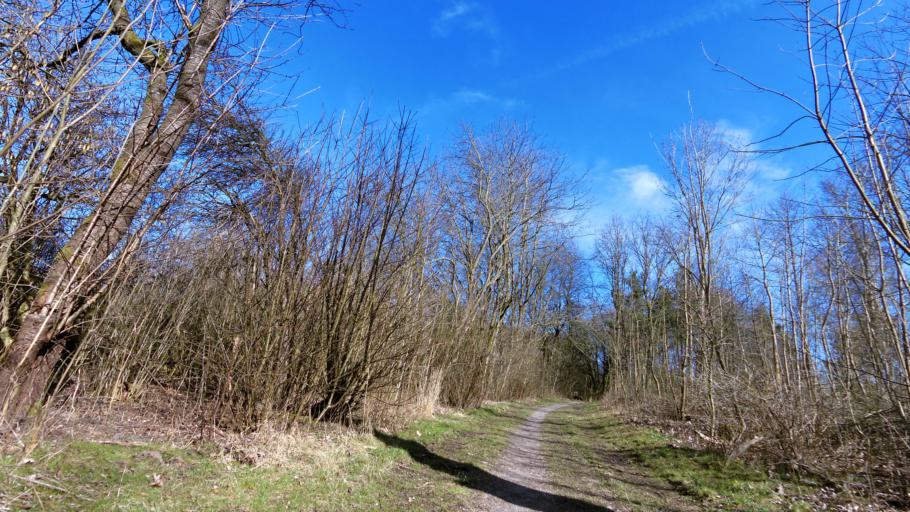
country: DK
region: Central Jutland
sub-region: Arhus Kommune
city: Stavtrup
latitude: 56.1709
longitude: 10.1265
